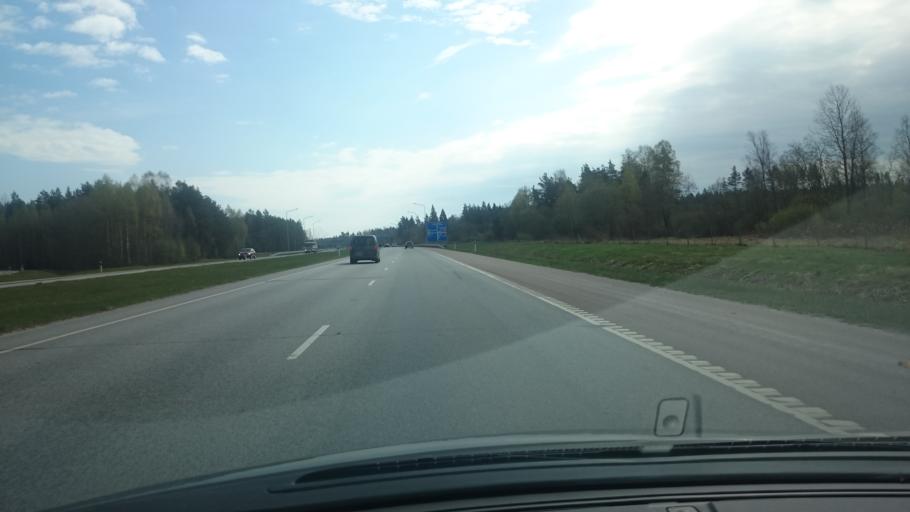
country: EE
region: Harju
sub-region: Raasiku vald
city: Raasiku
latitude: 59.4347
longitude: 25.1740
